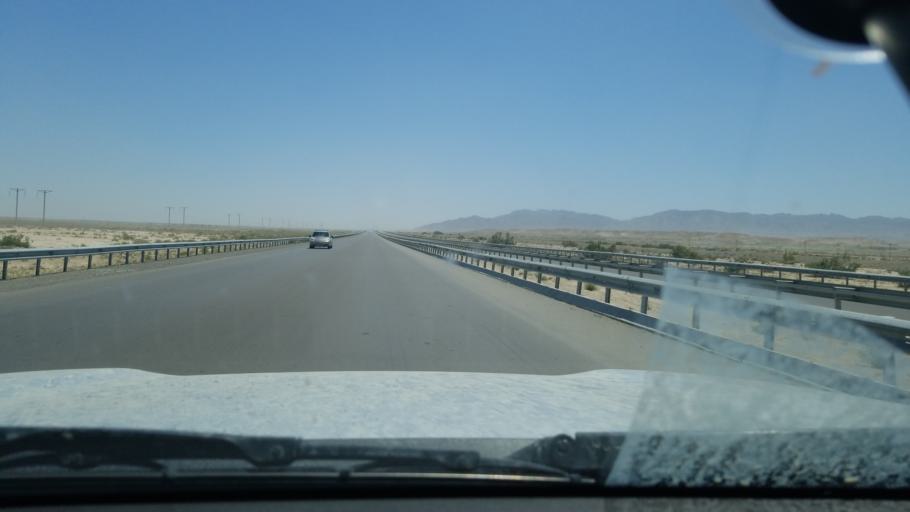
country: TM
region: Balkan
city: Gazanjyk
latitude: 39.2573
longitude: 55.3433
